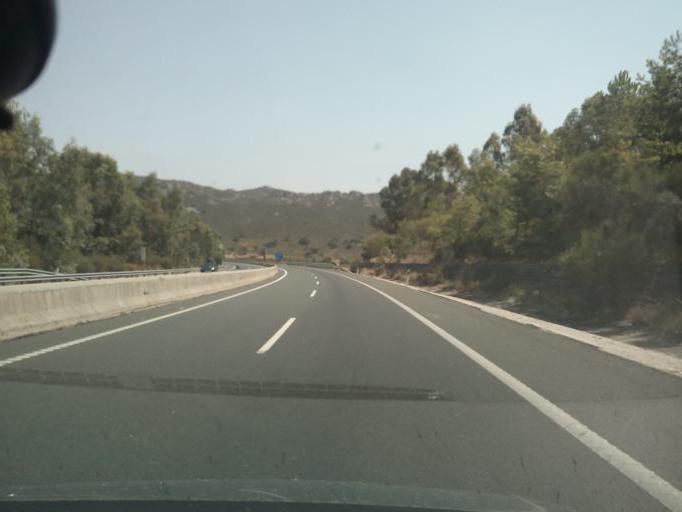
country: ES
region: Extremadura
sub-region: Provincia de Caceres
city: Higuera
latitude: 39.6986
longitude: -5.6928
